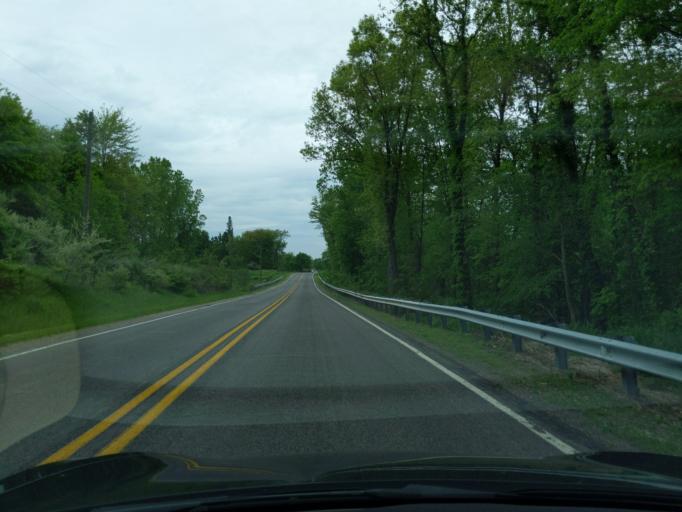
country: US
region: Michigan
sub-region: Ingham County
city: Leslie
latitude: 42.5107
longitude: -84.3562
